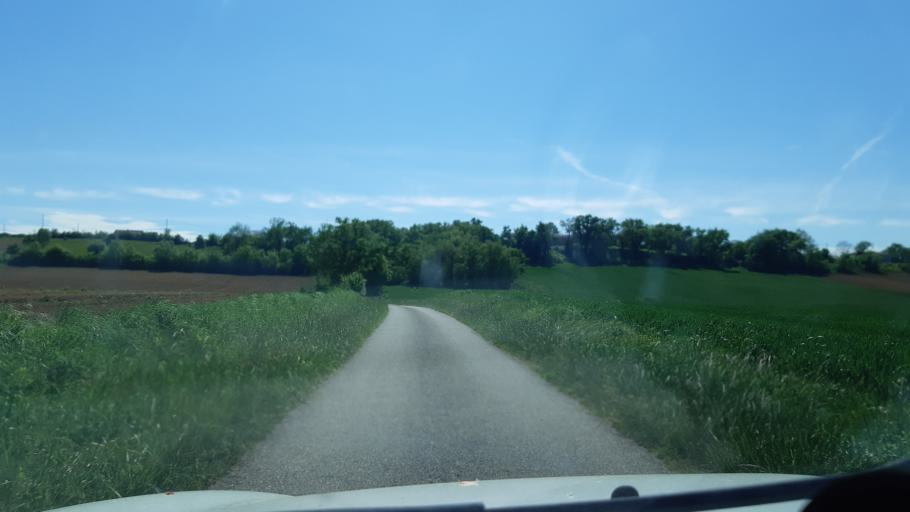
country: FR
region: Midi-Pyrenees
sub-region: Departement du Gers
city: Samatan
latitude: 43.5076
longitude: 1.0137
